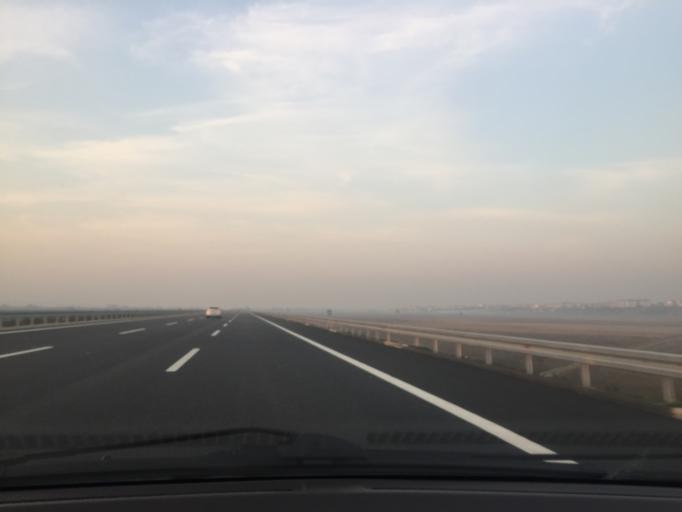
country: TR
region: Bursa
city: Karacabey
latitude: 40.2176
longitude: 28.3961
